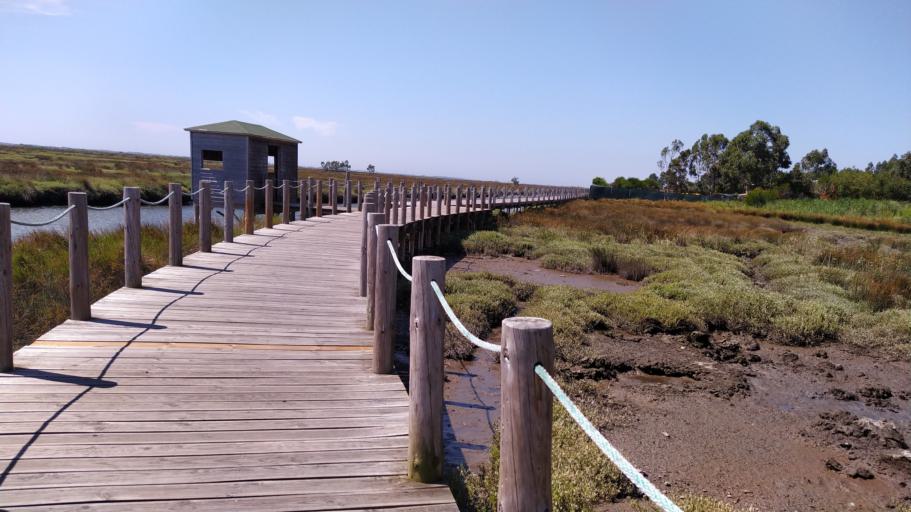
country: PT
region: Aveiro
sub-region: Aveiro
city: Aveiro
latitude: 40.6575
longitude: -8.6371
